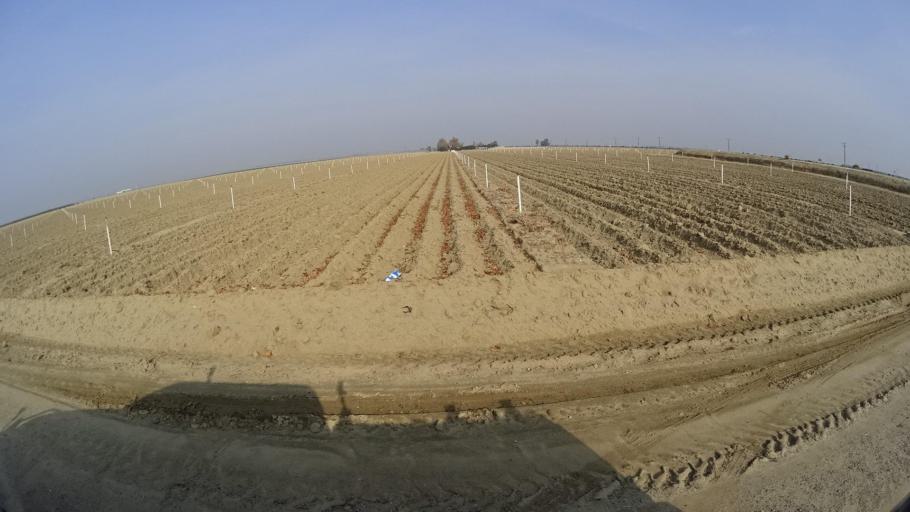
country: US
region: California
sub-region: Kern County
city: Weedpatch
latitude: 35.0955
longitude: -118.9868
